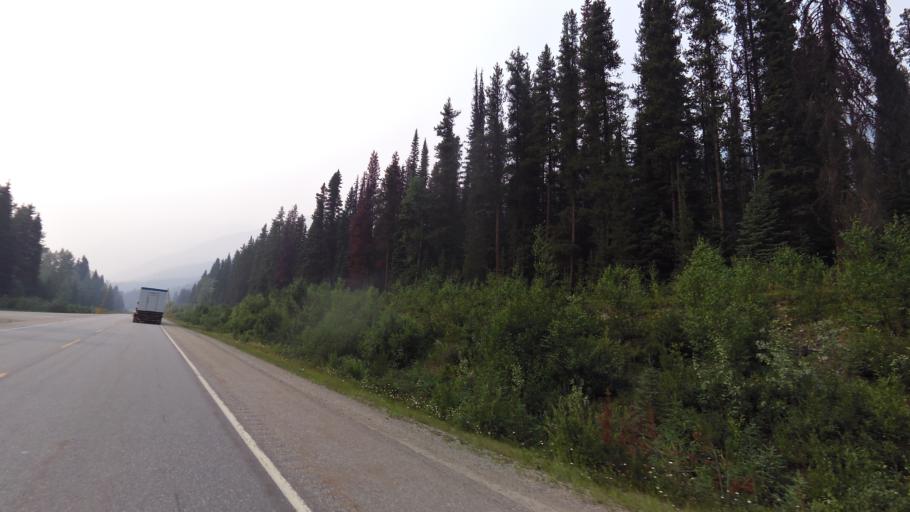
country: CA
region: Alberta
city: Grande Cache
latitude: 52.9956
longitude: -119.0215
